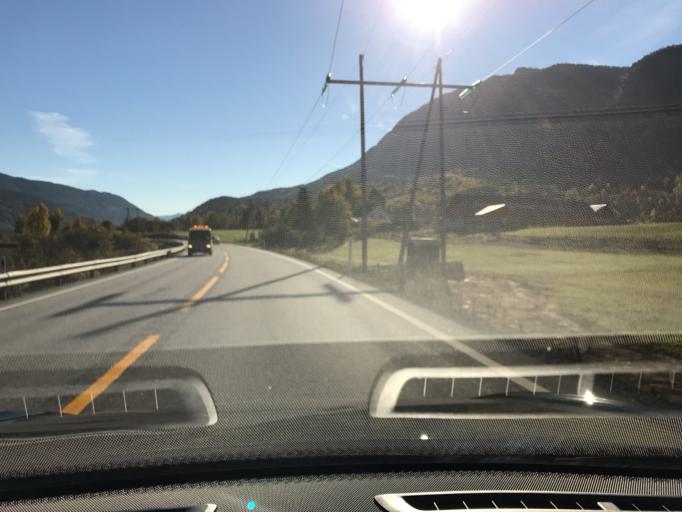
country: NO
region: Buskerud
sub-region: Nes
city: Nesbyen
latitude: 60.5652
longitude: 9.1162
